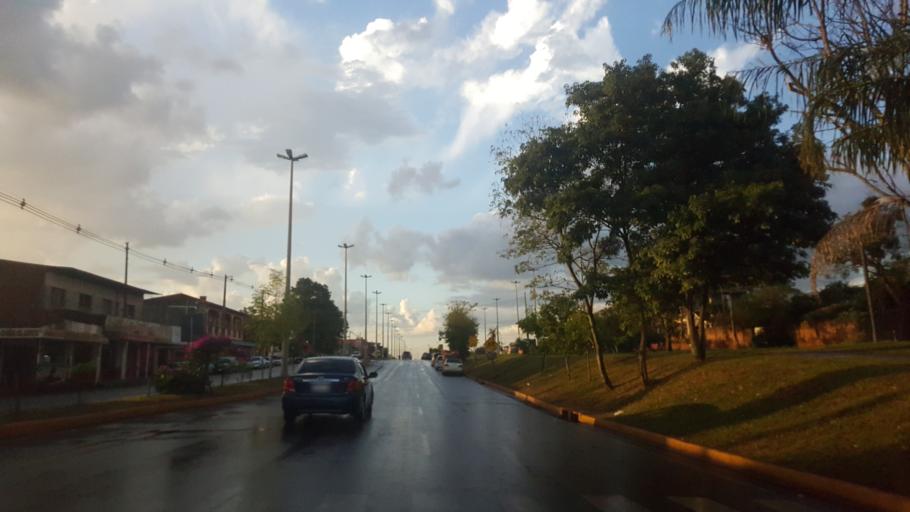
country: PY
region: Itapua
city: Encarnacion
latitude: -27.3586
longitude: -55.8587
